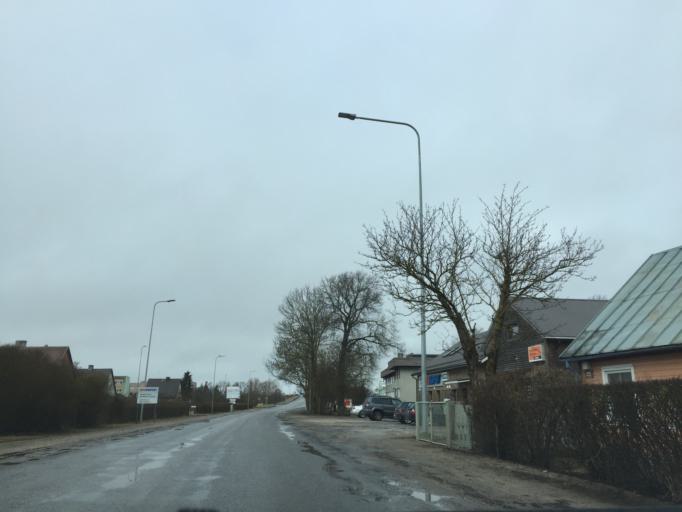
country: EE
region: Laeaene
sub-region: Haapsalu linn
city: Haapsalu
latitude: 58.9267
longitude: 23.5449
